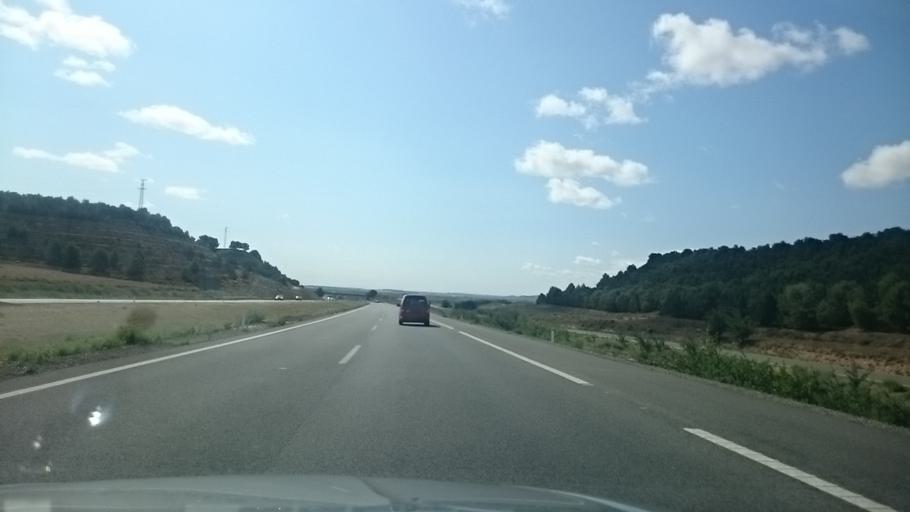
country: ES
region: Navarre
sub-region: Provincia de Navarra
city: Murchante
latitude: 42.0829
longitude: -1.7102
